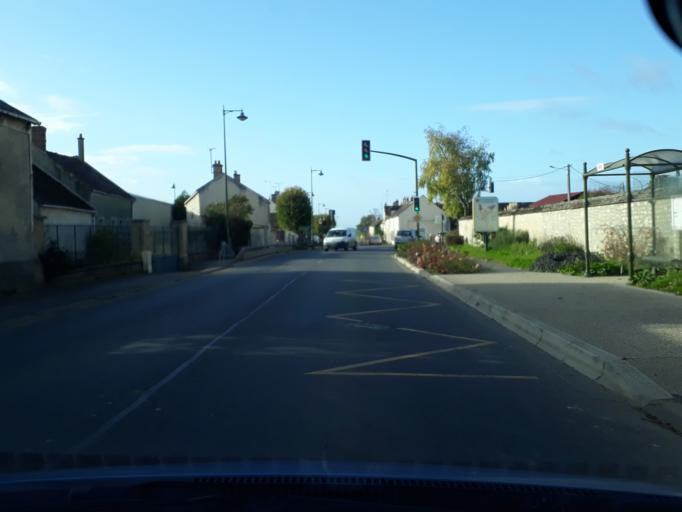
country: FR
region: Ile-de-France
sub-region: Departement de Seine-et-Marne
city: La Chapelle-la-Reine
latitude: 48.3157
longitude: 2.5689
